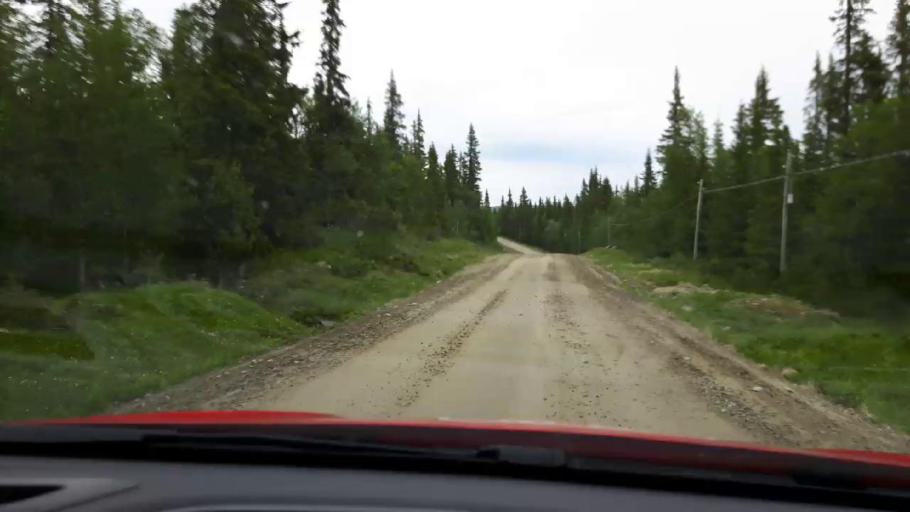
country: SE
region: Jaemtland
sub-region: Are Kommun
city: Are
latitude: 62.8263
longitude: 12.8120
